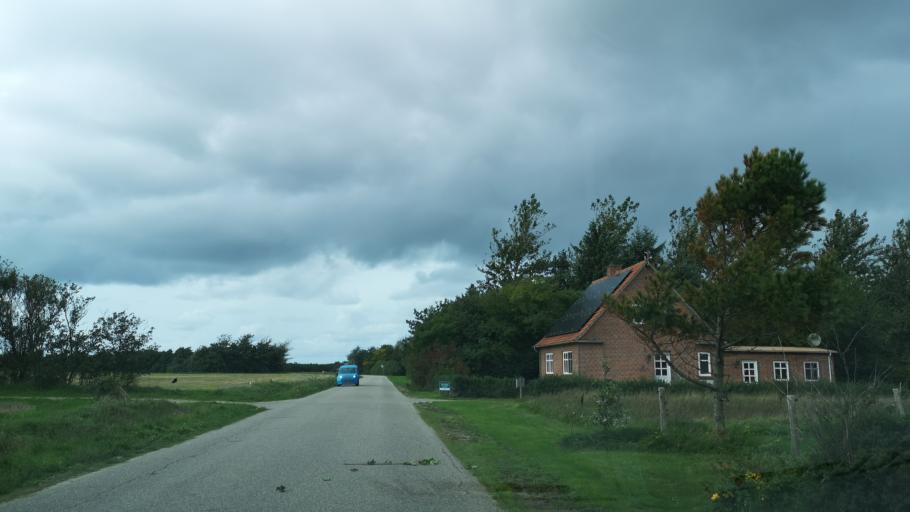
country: DK
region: South Denmark
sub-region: Varde Kommune
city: Oksbol
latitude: 55.8355
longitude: 8.3110
